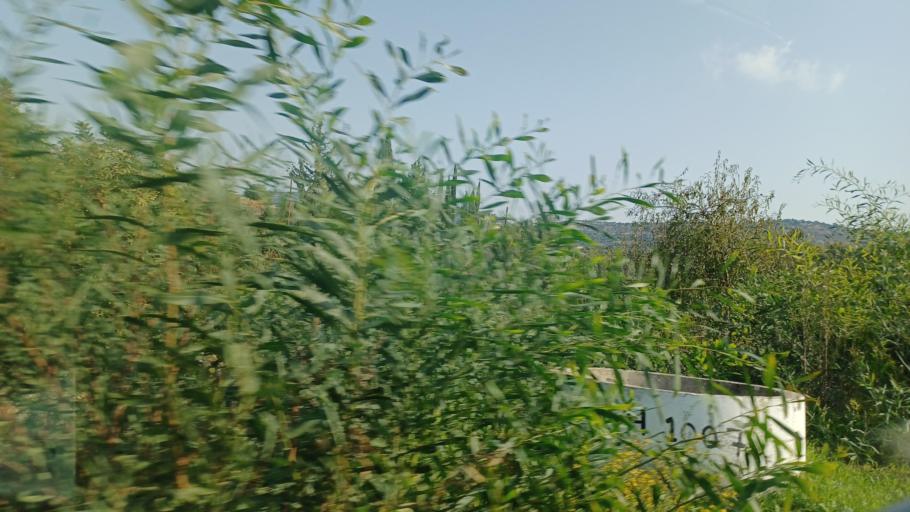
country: CY
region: Pafos
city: Polis
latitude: 34.9828
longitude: 32.4681
